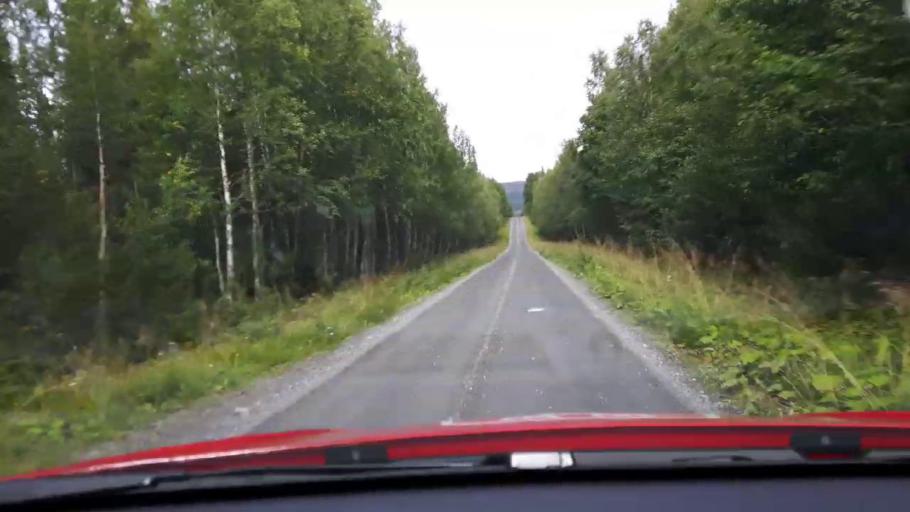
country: SE
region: Jaemtland
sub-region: Are Kommun
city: Are
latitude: 63.7946
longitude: 13.1081
